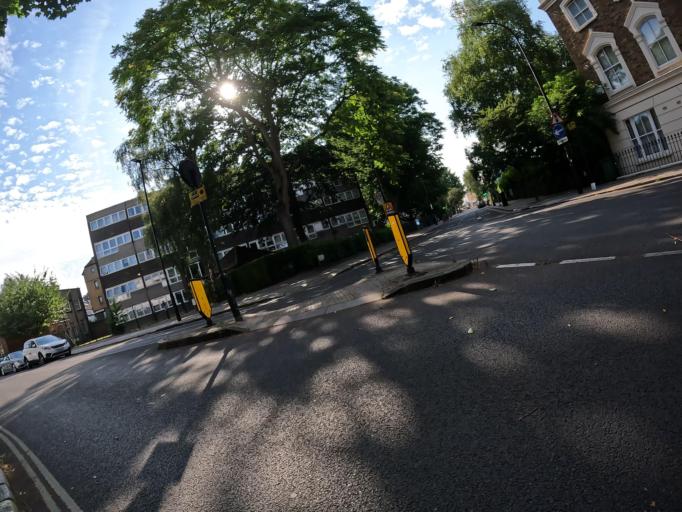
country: GB
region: England
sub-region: Greater London
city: Belsize Park
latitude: 51.5651
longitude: -0.1748
